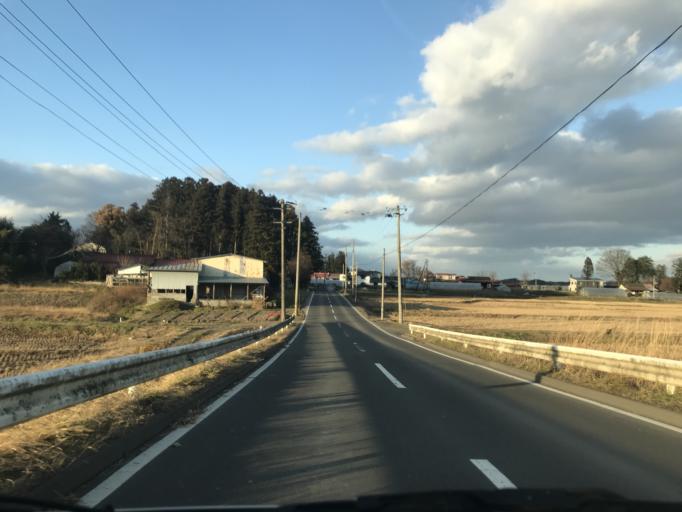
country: JP
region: Miyagi
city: Kogota
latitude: 38.6324
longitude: 141.0698
